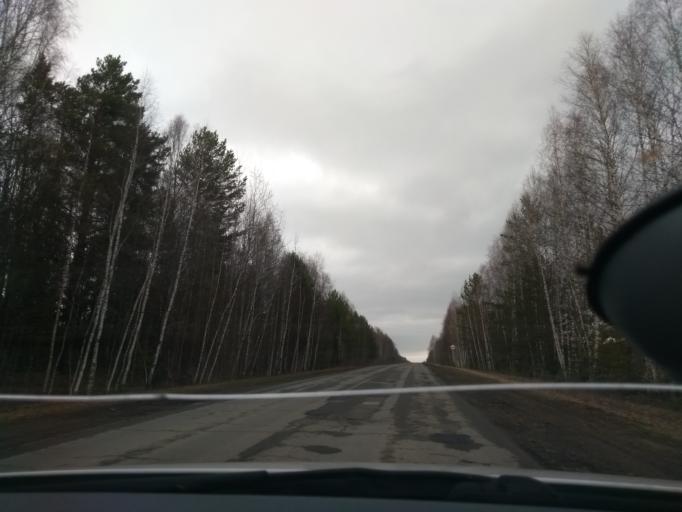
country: RU
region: Perm
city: Kungur
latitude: 57.3573
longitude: 56.8106
